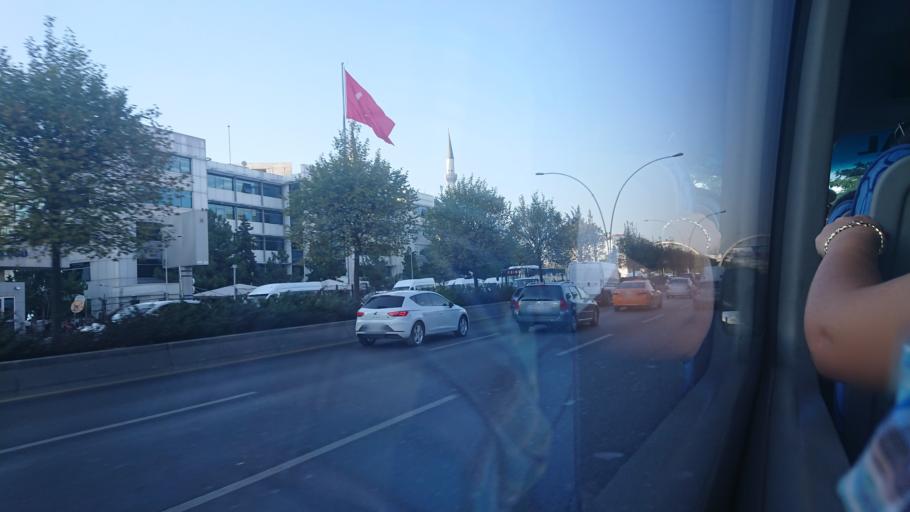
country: TR
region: Ankara
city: Ankara
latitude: 39.9397
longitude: 32.8260
